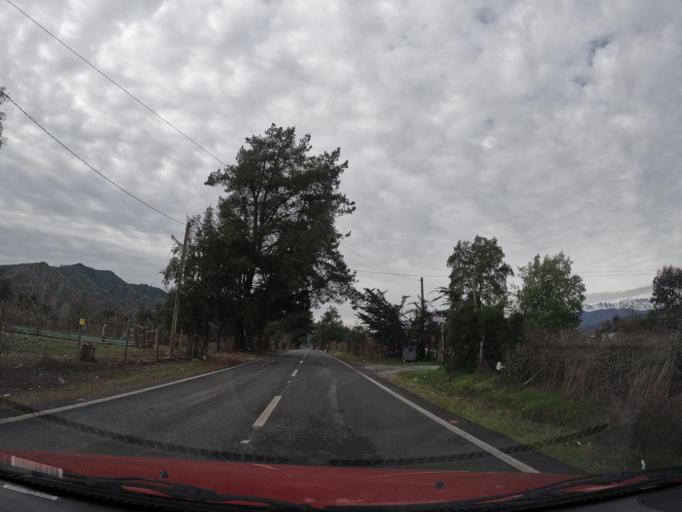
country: CL
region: Maule
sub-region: Provincia de Linares
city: Linares
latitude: -35.9261
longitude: -71.4204
